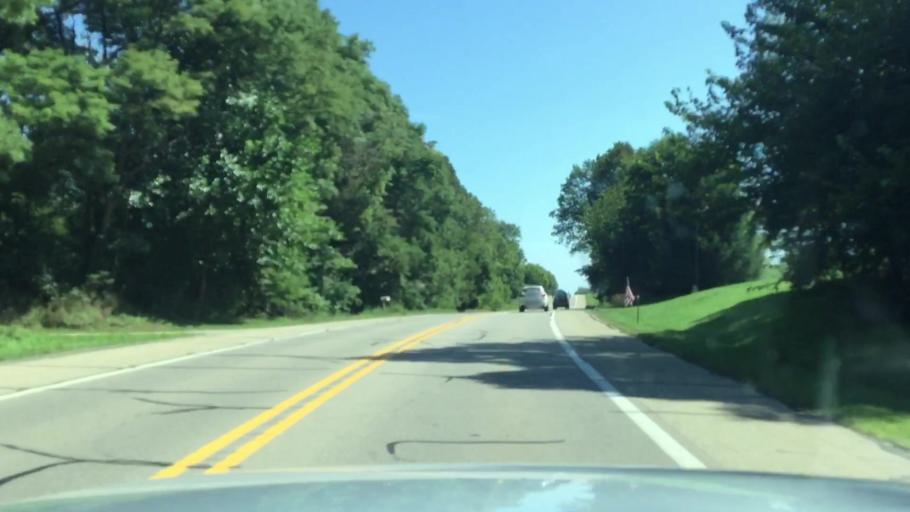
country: US
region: Michigan
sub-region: Washtenaw County
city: Manchester
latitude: 42.0724
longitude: -84.0768
